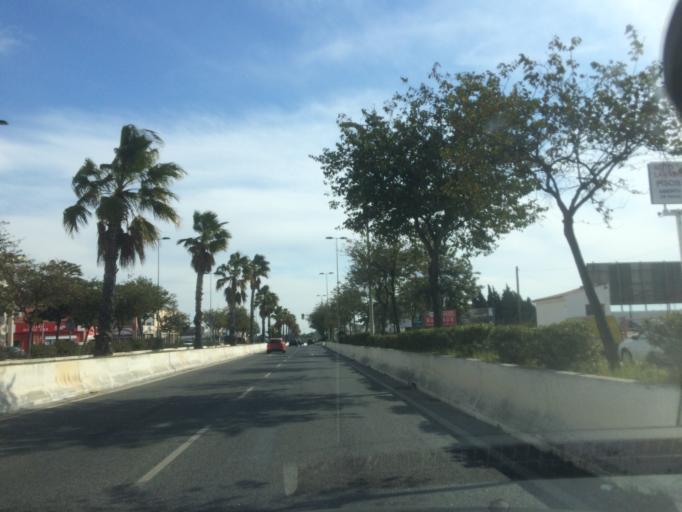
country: ES
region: Andalusia
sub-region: Provincia de Malaga
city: Torremolinos
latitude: 36.6600
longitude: -4.4970
